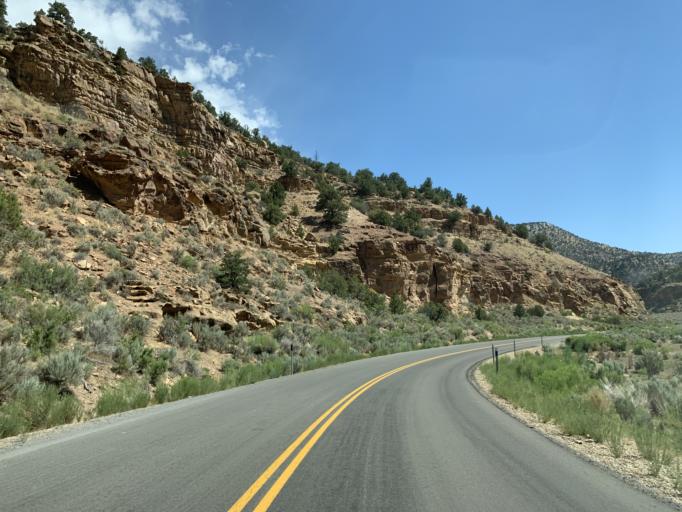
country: US
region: Utah
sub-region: Carbon County
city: East Carbon City
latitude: 39.7810
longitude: -110.4227
